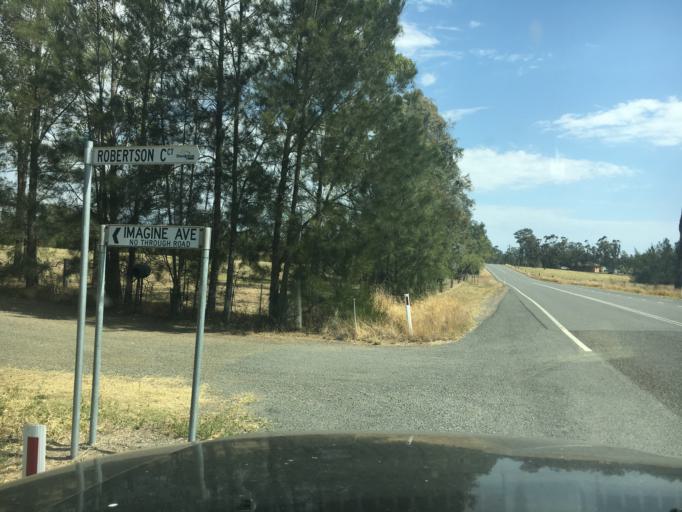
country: AU
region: New South Wales
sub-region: Singleton
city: Singleton
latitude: -32.5456
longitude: 151.2421
